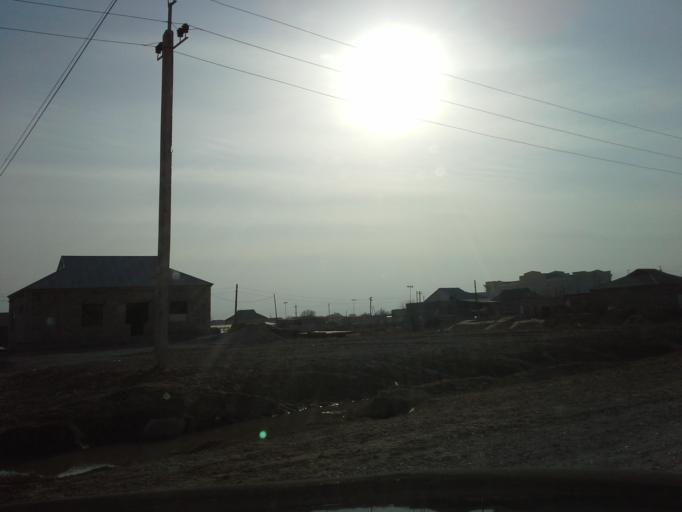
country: TM
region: Ahal
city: Abadan
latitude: 38.1783
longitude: 58.0474
